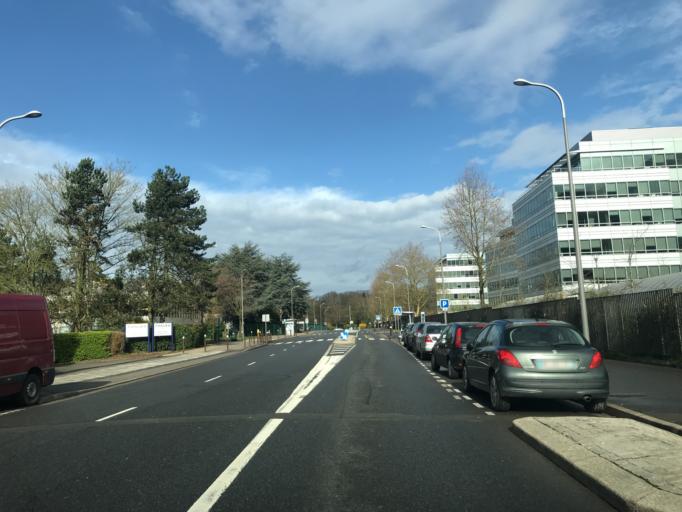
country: FR
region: Ile-de-France
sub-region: Departement des Yvelines
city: Velizy-Villacoublay
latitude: 48.7854
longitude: 2.2120
